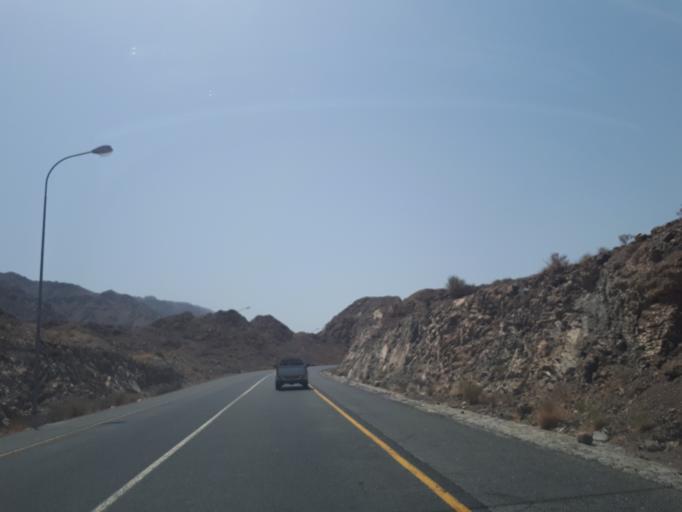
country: OM
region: Muhafazat ad Dakhiliyah
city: Sufalat Sama'il
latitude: 23.1995
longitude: 58.0834
